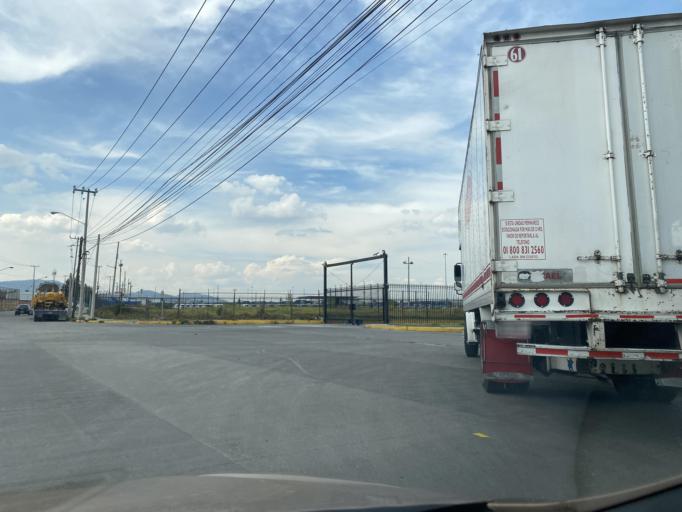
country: IN
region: Karnataka
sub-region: Dakshina Kannada
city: Puttur
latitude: 12.7530
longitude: 75.1977
